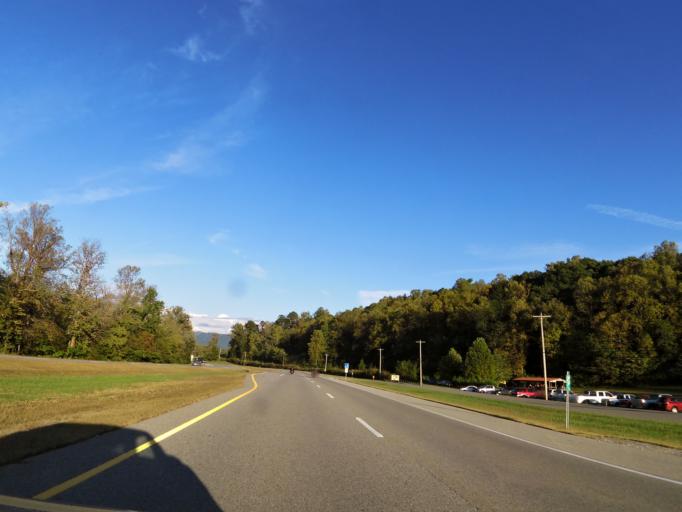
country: US
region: Tennessee
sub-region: Blount County
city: Wildwood
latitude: 35.6792
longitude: -83.7816
